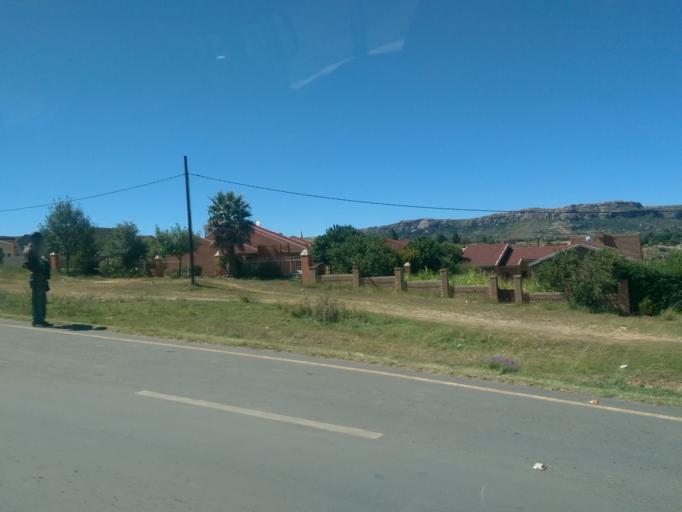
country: LS
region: Maseru
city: Maseru
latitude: -29.3730
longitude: 27.5449
